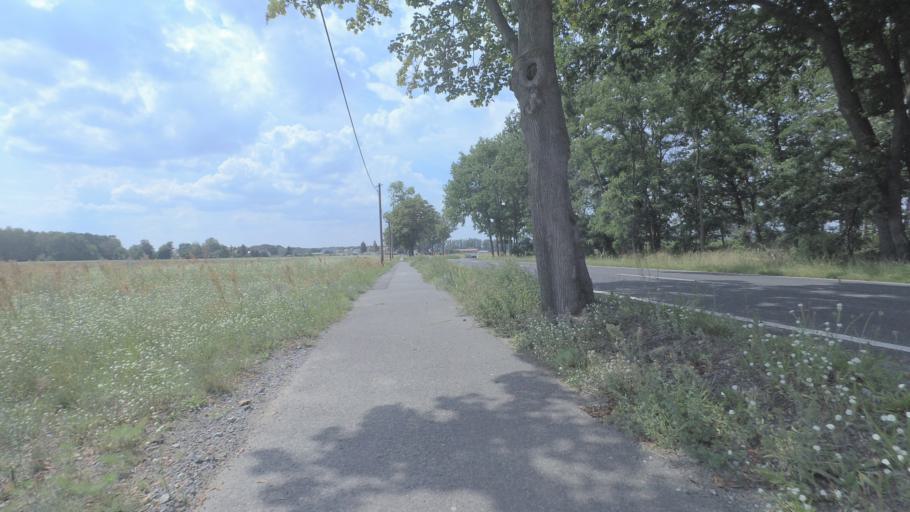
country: DE
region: Brandenburg
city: Luckenwalde
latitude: 52.1154
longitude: 13.2154
